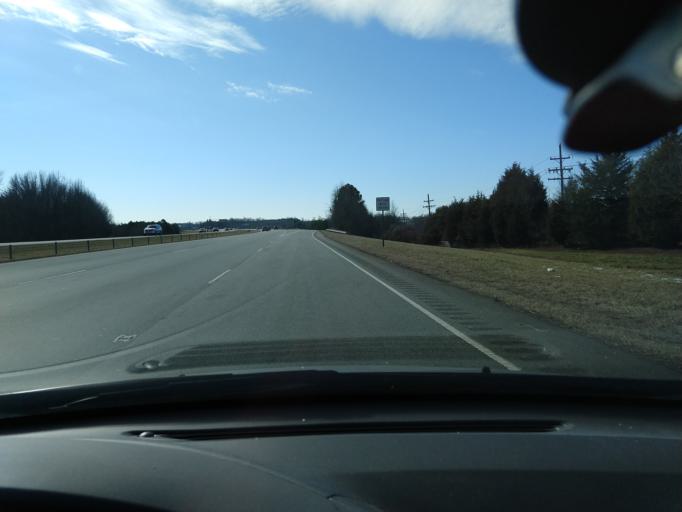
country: US
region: North Carolina
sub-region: Guilford County
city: Oak Ridge
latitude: 36.1004
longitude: -79.9663
